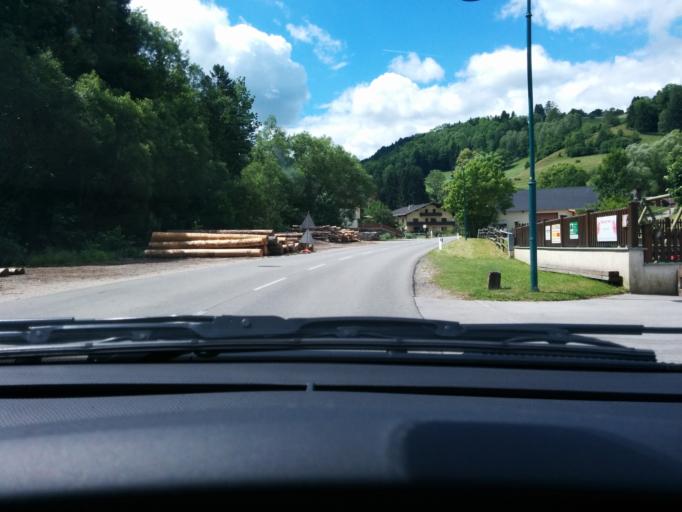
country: AT
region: Lower Austria
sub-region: Politischer Bezirk Wiener Neustadt
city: Miesenbach
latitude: 47.8455
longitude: 15.9838
